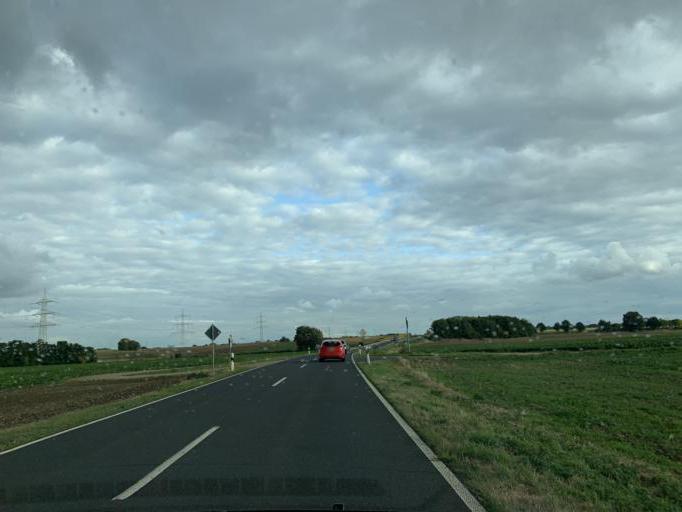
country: DE
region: North Rhine-Westphalia
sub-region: Regierungsbezirk Koln
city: Aldenhoven
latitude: 50.9250
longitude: 6.3044
